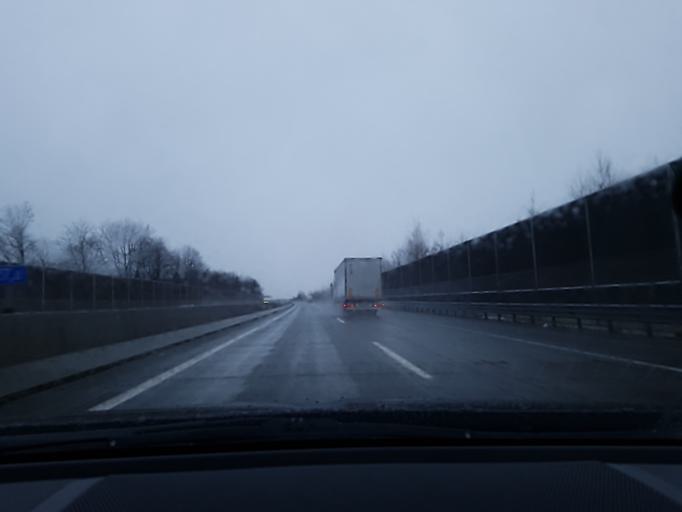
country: AT
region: Salzburg
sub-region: Politischer Bezirk Hallein
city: Golling an der Salzach
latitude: 47.5992
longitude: 13.1507
